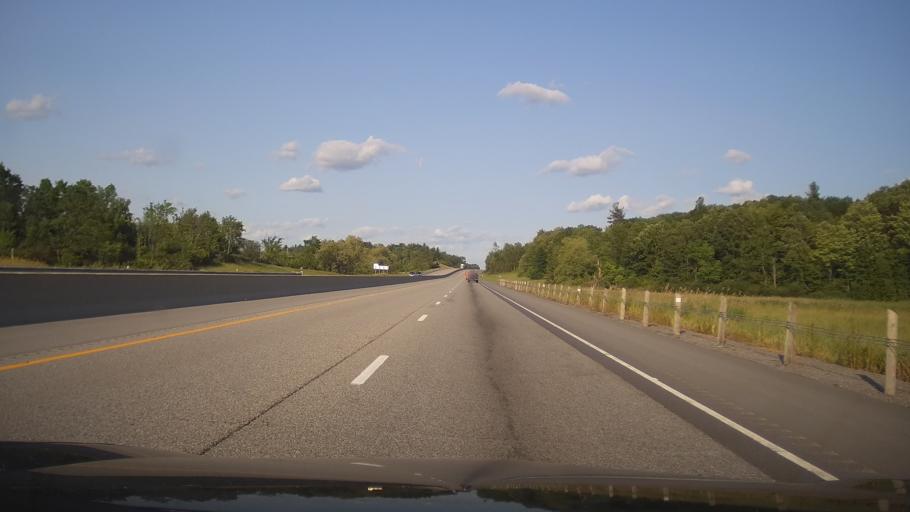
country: CA
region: Ontario
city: Gananoque
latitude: 44.3250
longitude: -76.3067
